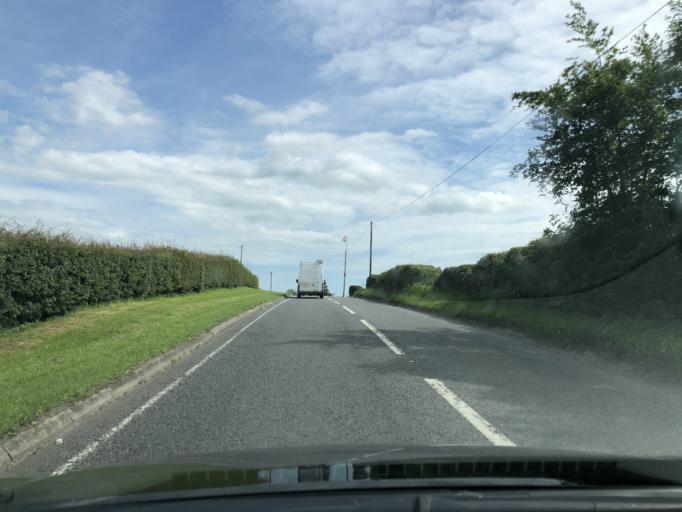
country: GB
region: Northern Ireland
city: Ballynahinch
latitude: 54.4210
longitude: -5.9162
